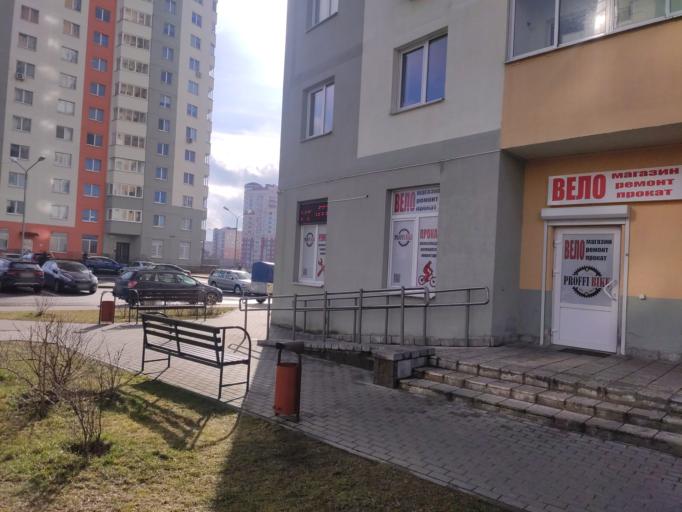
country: BY
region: Minsk
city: Novoye Medvezhino
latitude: 53.8546
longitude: 27.4791
